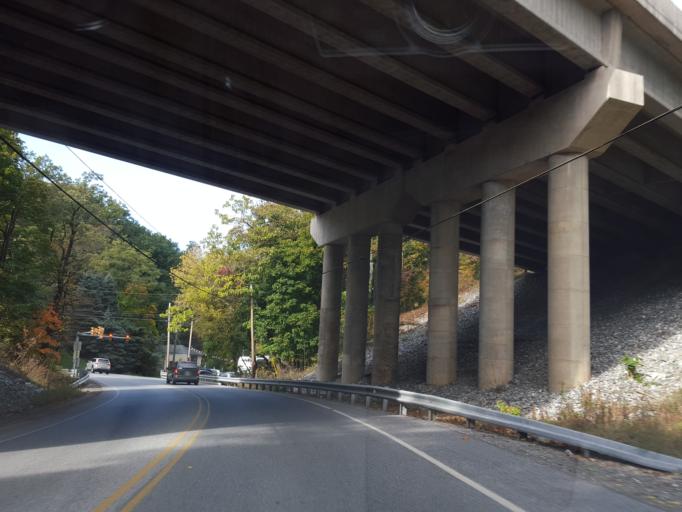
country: US
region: Pennsylvania
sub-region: York County
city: Valley View
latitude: 39.9328
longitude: -76.7107
